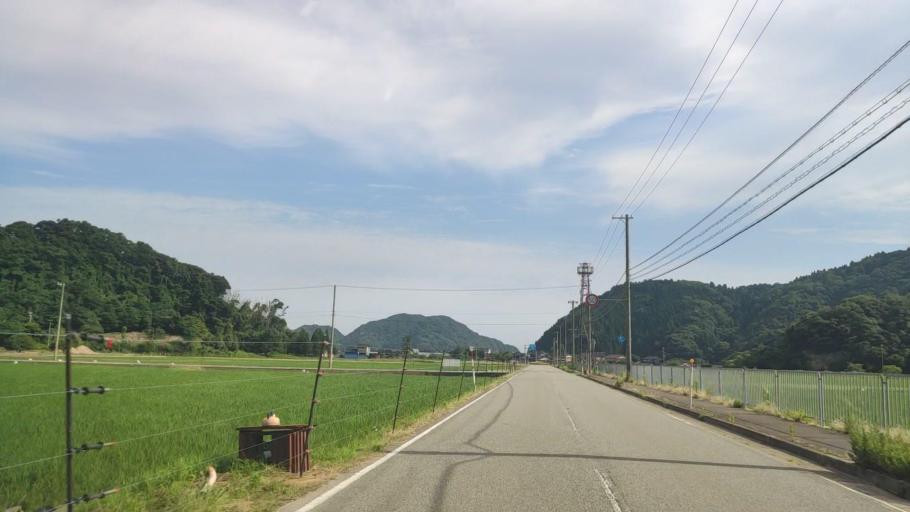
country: JP
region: Hyogo
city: Toyooka
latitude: 35.6297
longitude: 134.8409
